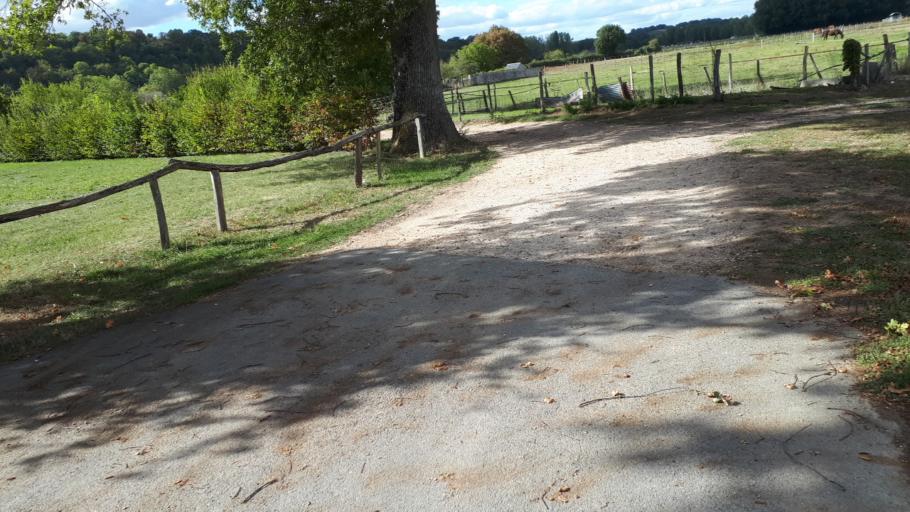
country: FR
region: Centre
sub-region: Departement du Loir-et-Cher
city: Villiers-sur-Loir
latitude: 47.7886
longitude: 0.9617
